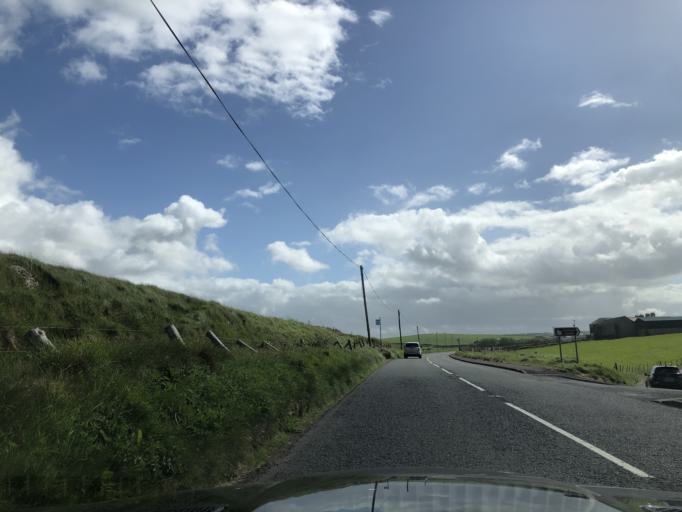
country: GB
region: Northern Ireland
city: Bushmills
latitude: 55.2114
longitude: -6.5758
